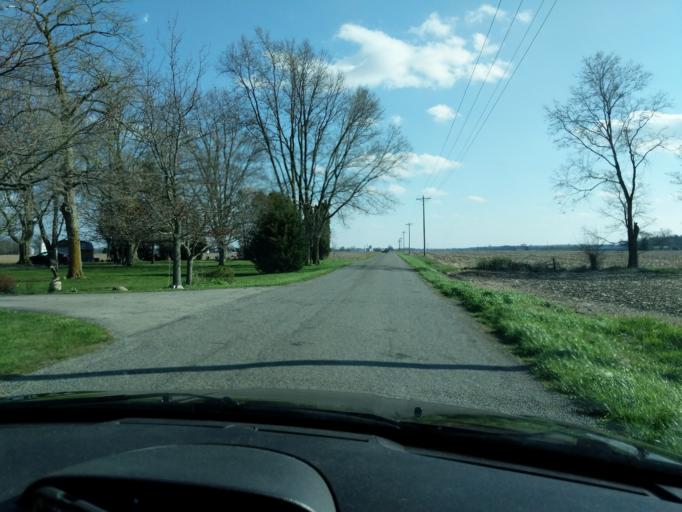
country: US
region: Ohio
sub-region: Champaign County
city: Urbana
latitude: 40.1268
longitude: -83.8112
